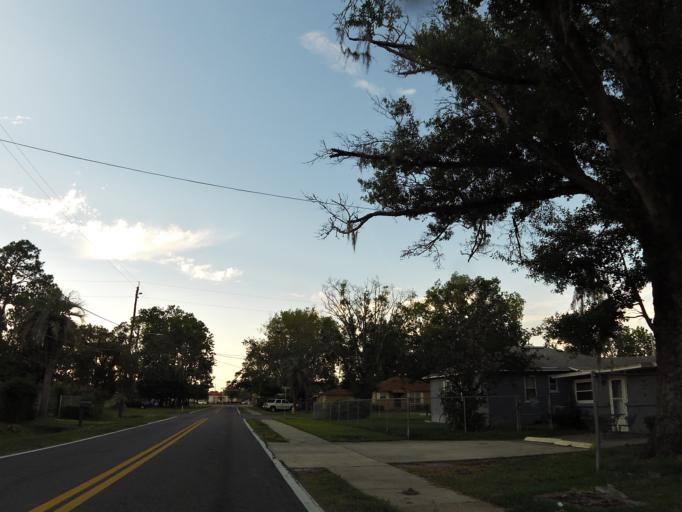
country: US
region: Florida
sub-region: Duval County
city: Jacksonville
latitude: 30.3070
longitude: -81.7394
